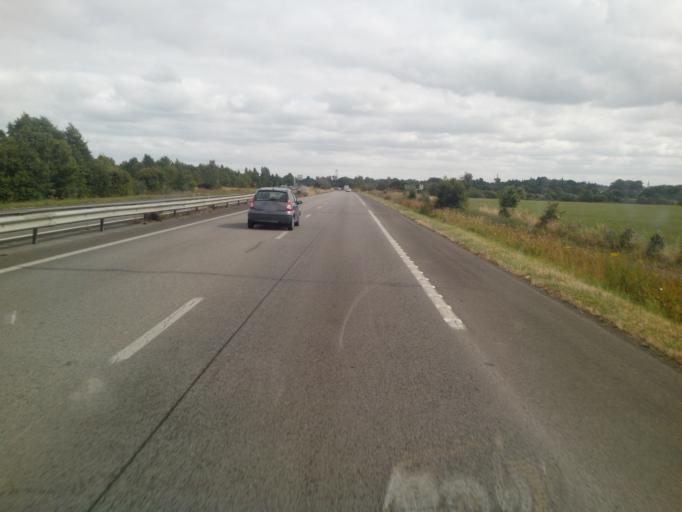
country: FR
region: Pays de la Loire
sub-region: Departement de la Loire-Atlantique
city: Heric
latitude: 47.4395
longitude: -1.6401
